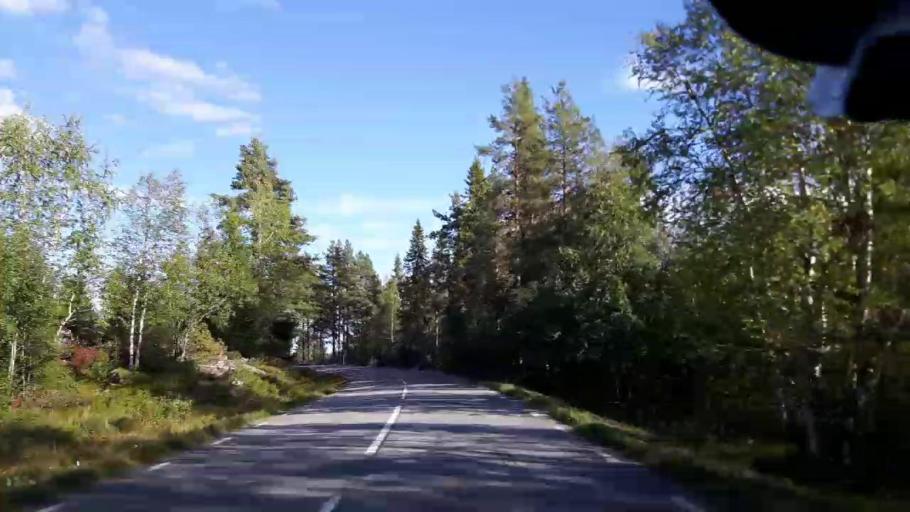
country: SE
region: Jaemtland
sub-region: Stroemsunds Kommun
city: Stroemsund
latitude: 63.3874
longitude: 15.5647
